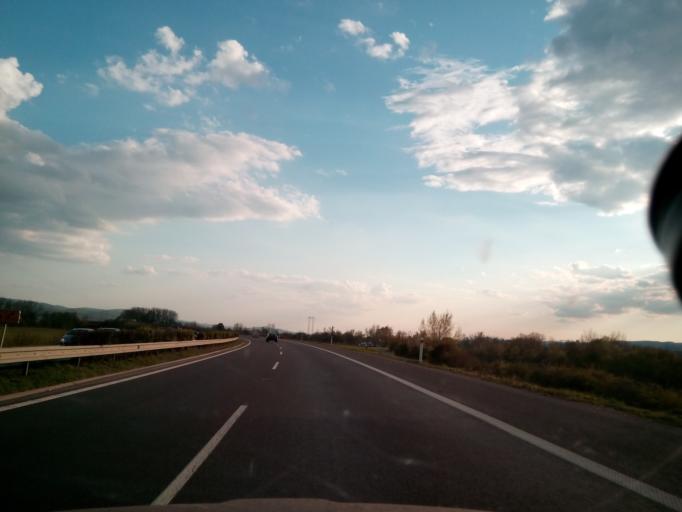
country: SK
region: Nitriansky
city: Ilava
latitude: 49.0424
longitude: 18.2772
